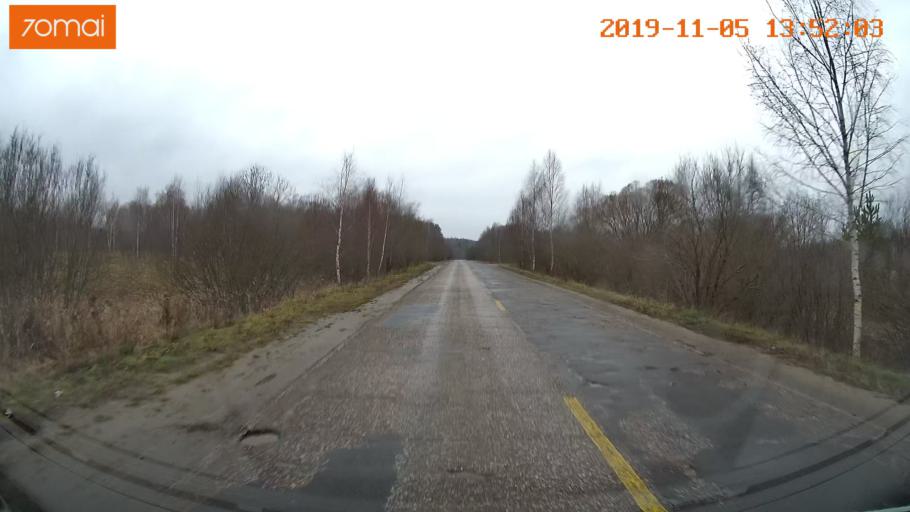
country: RU
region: Ivanovo
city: Kaminskiy
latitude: 57.0264
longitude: 41.3921
